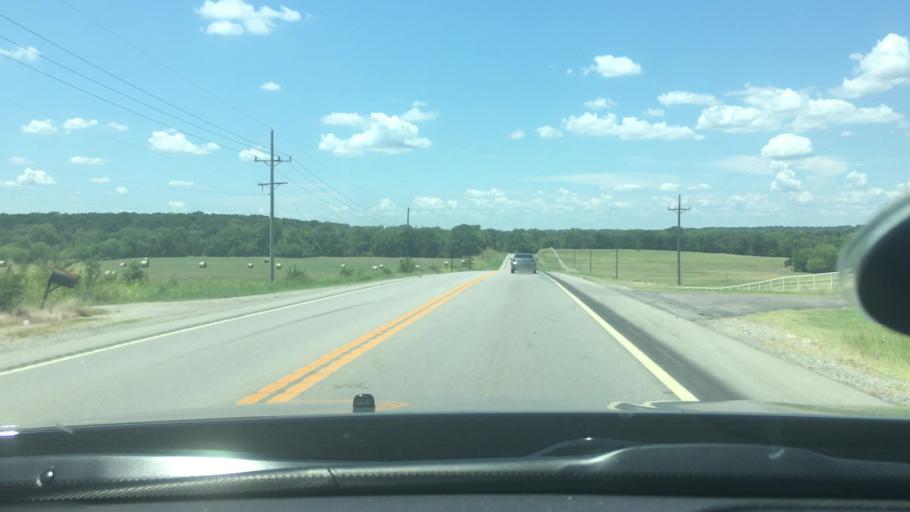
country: US
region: Oklahoma
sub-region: Bryan County
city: Durant
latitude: 33.9975
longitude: -96.2945
